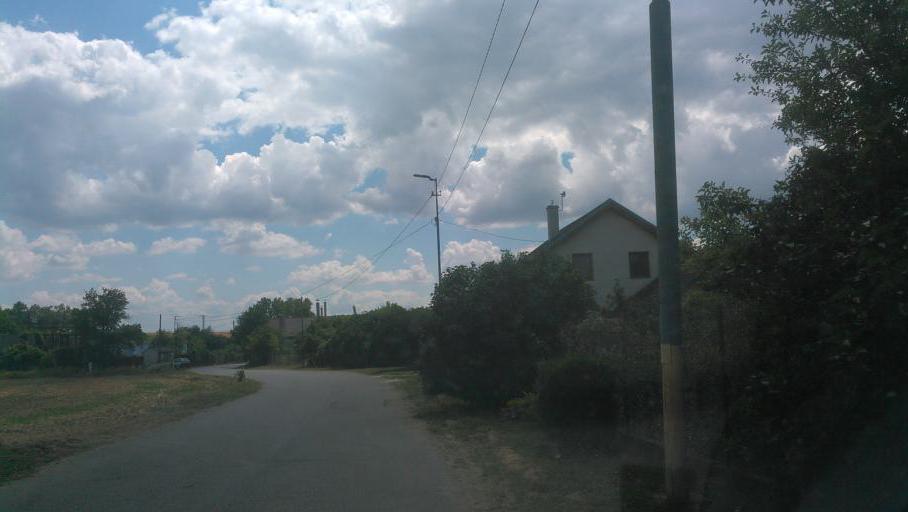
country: SK
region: Trnavsky
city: Vrbove
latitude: 48.6257
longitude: 17.7252
